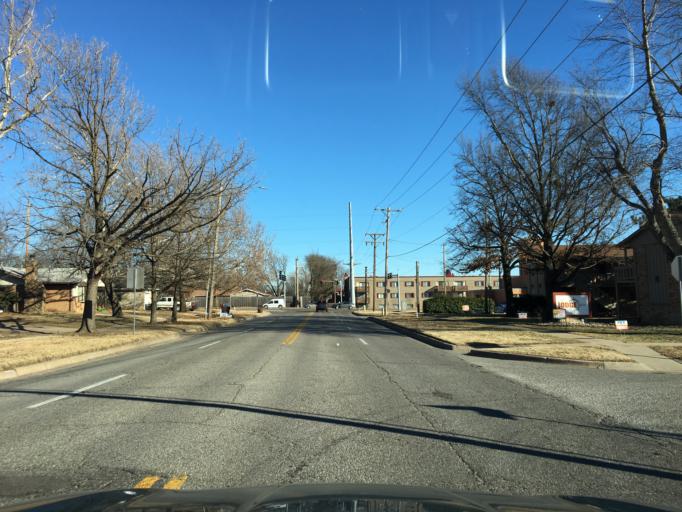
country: US
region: Kansas
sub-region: Sedgwick County
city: Bellaire
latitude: 37.6720
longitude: -97.2459
